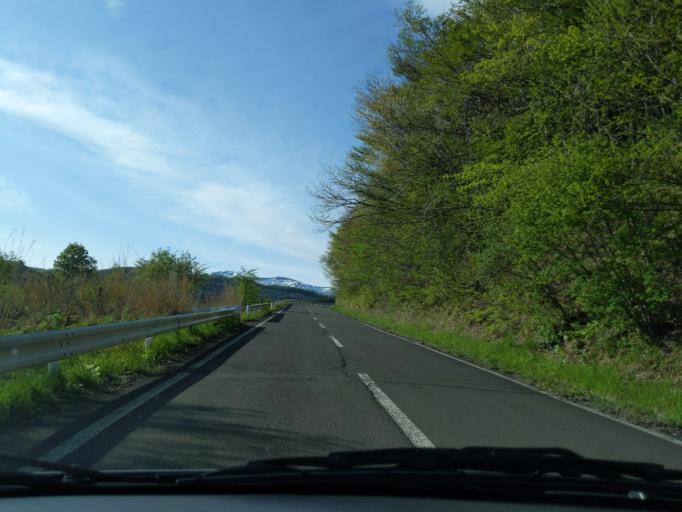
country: JP
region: Iwate
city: Ichinoseki
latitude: 38.8890
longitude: 140.8574
